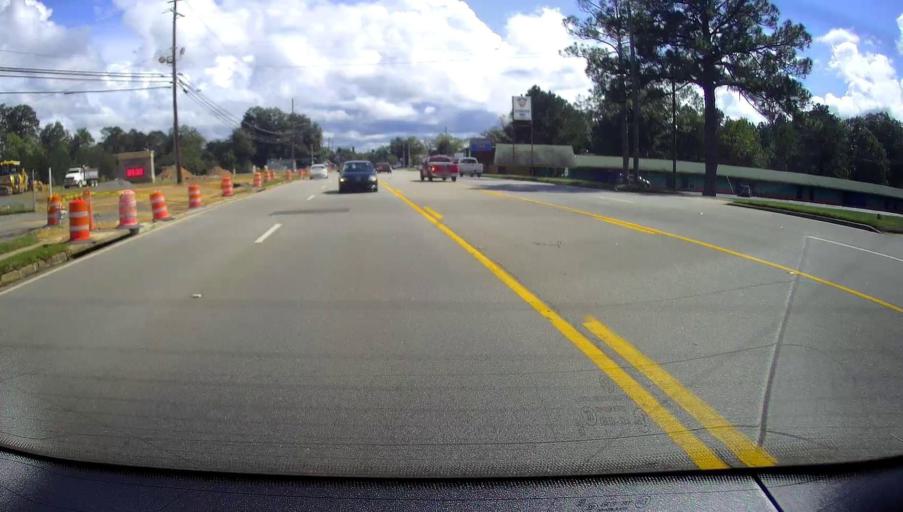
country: US
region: Georgia
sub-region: Baldwin County
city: Milledgeville
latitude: 33.0976
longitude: -83.2443
